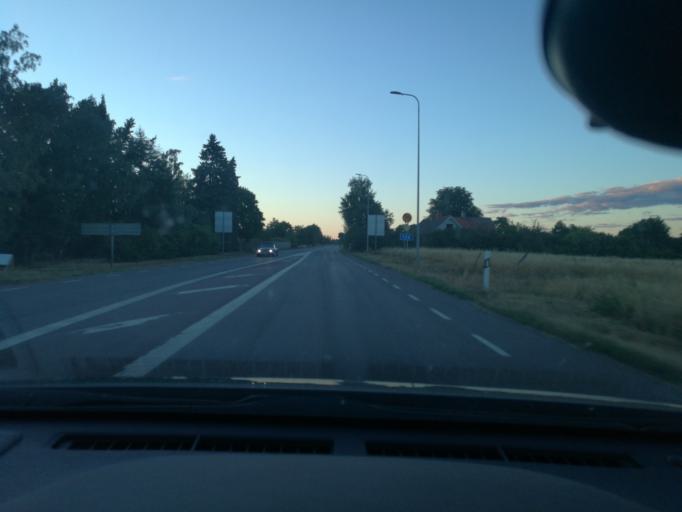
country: SE
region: Kalmar
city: Faerjestaden
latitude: 56.6823
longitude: 16.5220
